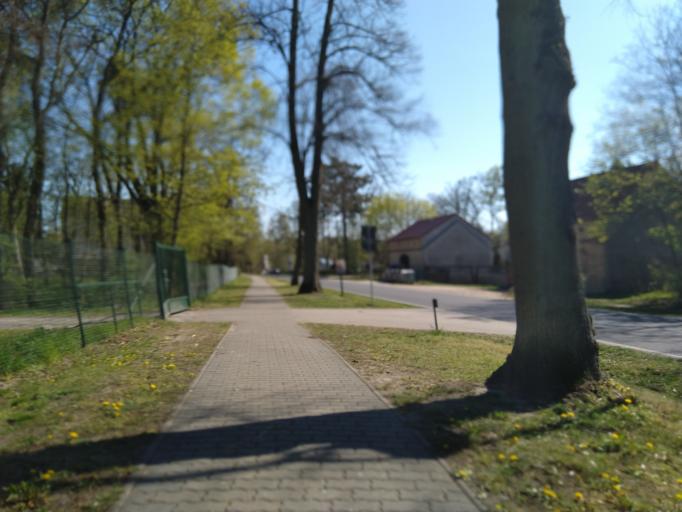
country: DE
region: Brandenburg
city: Biesenthal
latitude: 52.7682
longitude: 13.6164
